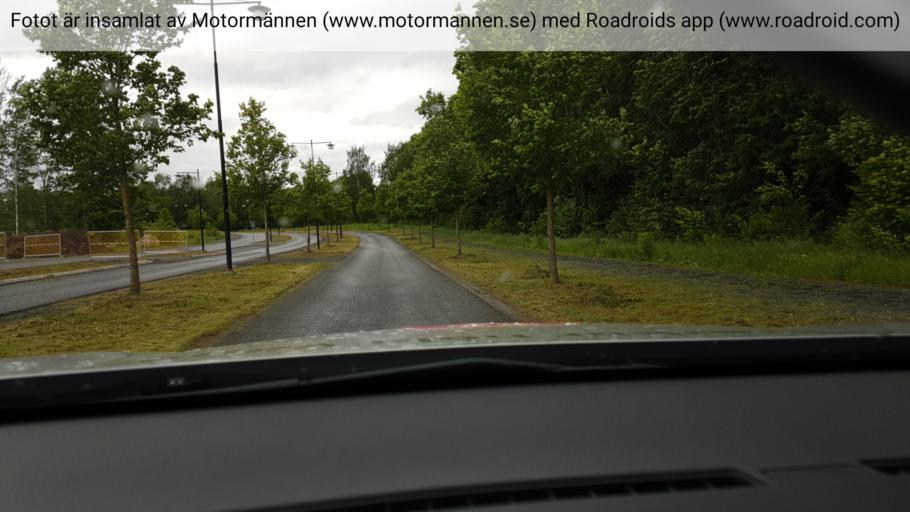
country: SE
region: Vaestra Goetaland
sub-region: Skovde Kommun
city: Skoevde
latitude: 58.4152
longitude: 13.8943
